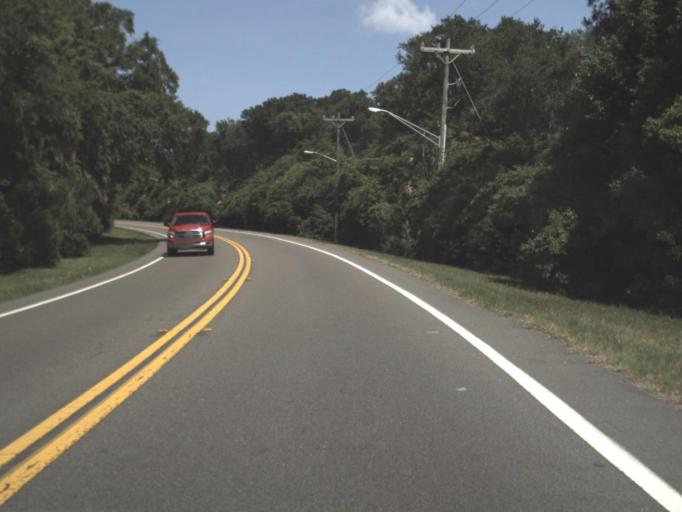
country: US
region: Florida
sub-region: Duval County
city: Atlantic Beach
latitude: 30.3977
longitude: -81.5018
